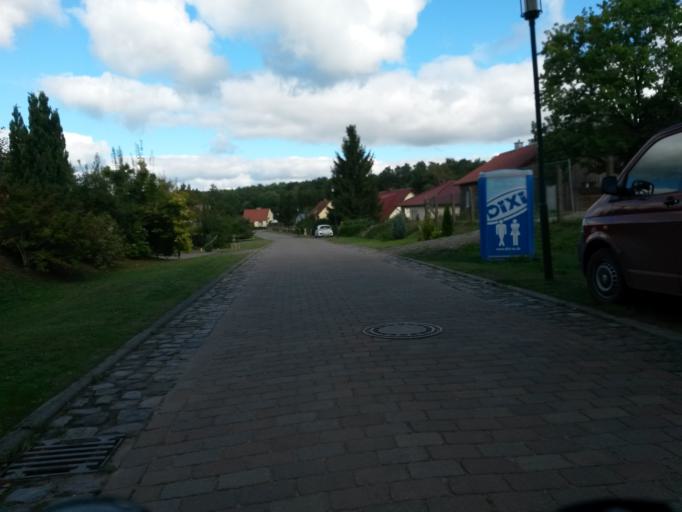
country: DE
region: Brandenburg
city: Templin
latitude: 53.2125
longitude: 13.5155
